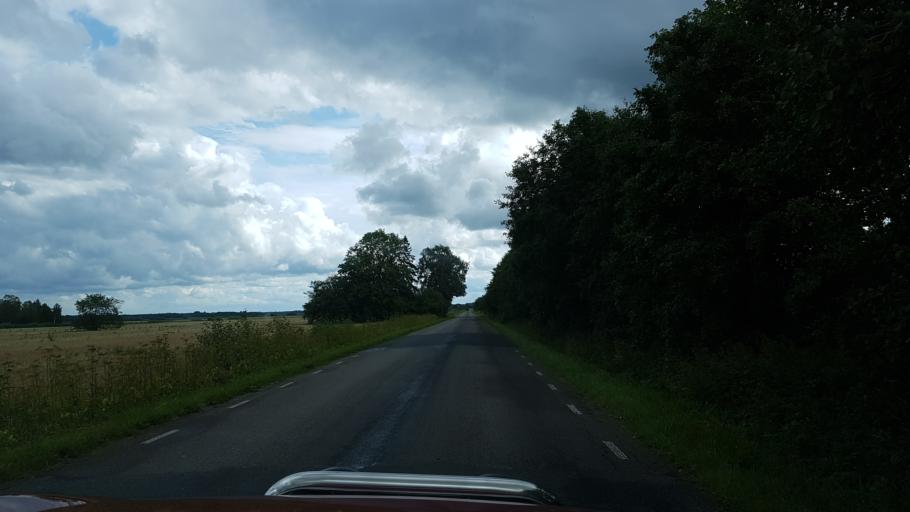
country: EE
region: Laeaene
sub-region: Lihula vald
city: Lihula
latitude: 58.7208
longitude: 23.9739
